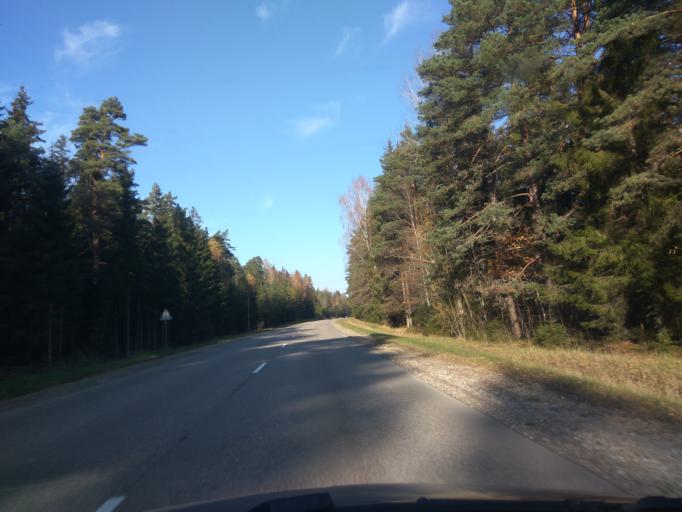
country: LV
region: Ventspils Rajons
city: Piltene
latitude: 57.0900
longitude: 21.7786
